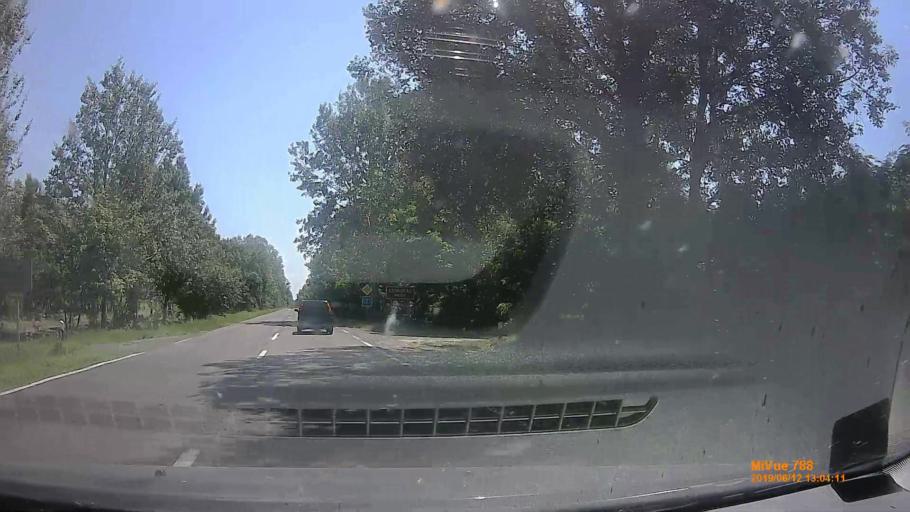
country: HU
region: Csongrad
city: Pusztaszer
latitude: 46.5535
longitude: 19.9482
